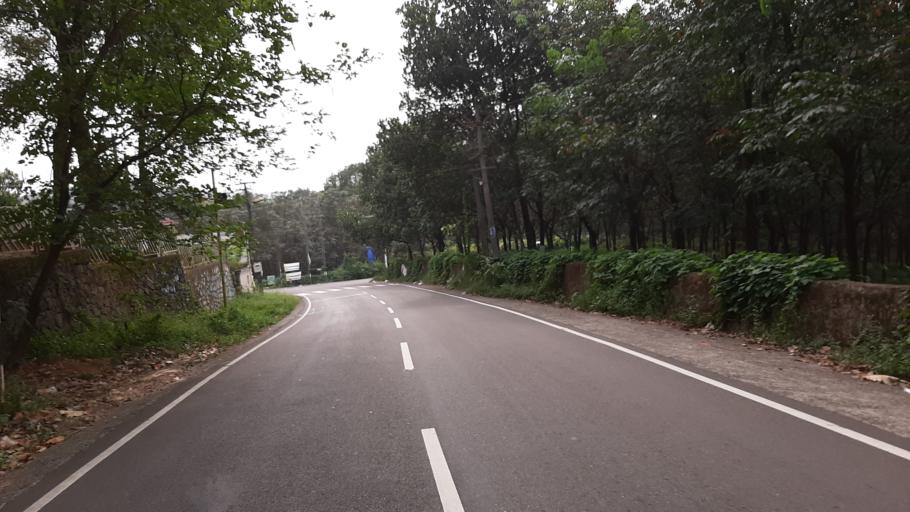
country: IN
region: Kerala
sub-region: Pattanamtitta
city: Pathanamthitta
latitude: 9.4554
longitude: 76.8669
